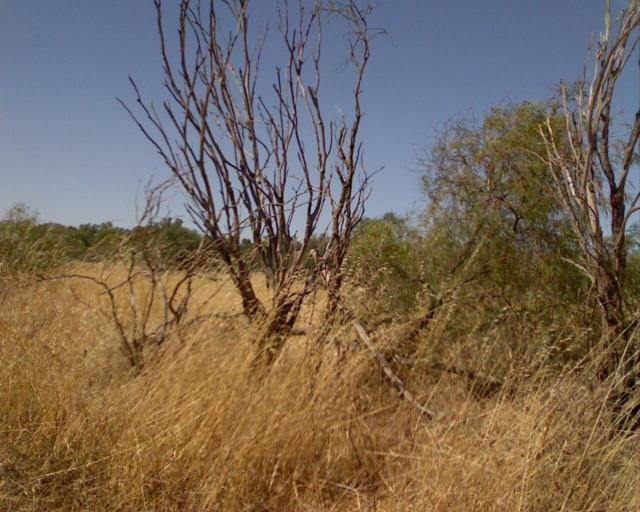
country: AU
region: Western Australia
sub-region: Irwin
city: Dongara
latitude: -29.1878
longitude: 115.4387
